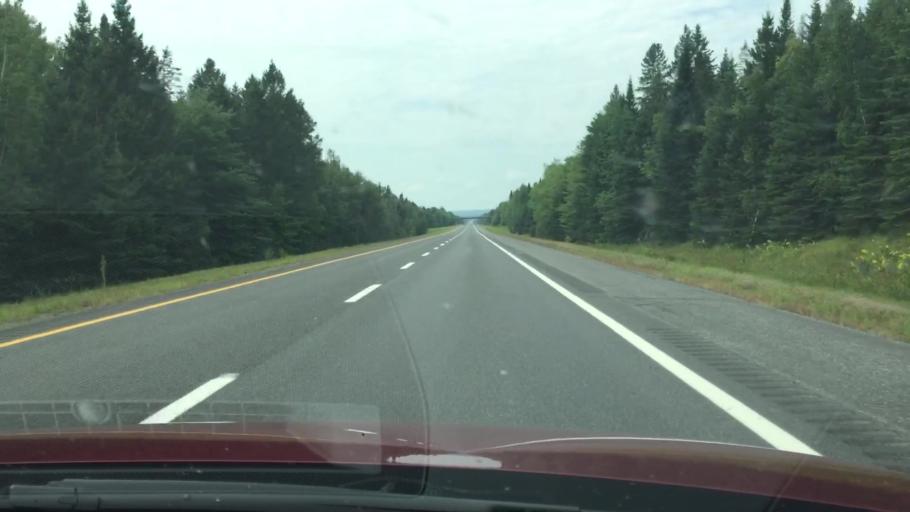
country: US
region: Maine
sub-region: Aroostook County
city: Houlton
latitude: 46.1417
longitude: -67.9465
